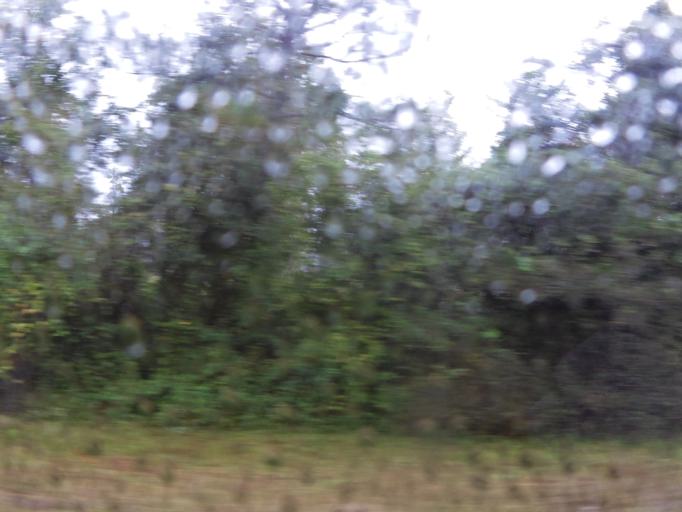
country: US
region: Florida
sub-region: Baker County
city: Macclenny
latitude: 30.3724
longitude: -82.1400
